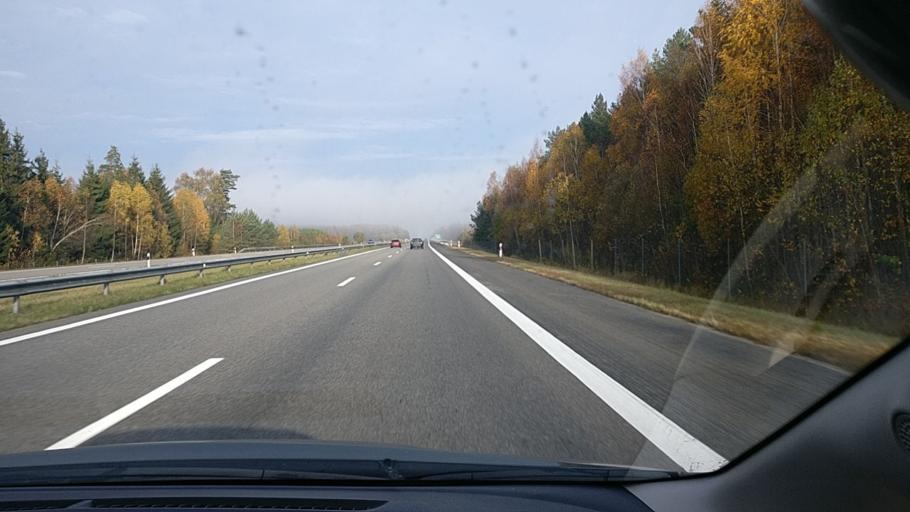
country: LT
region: Vilnius County
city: Ukmerge
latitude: 55.4931
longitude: 24.6257
